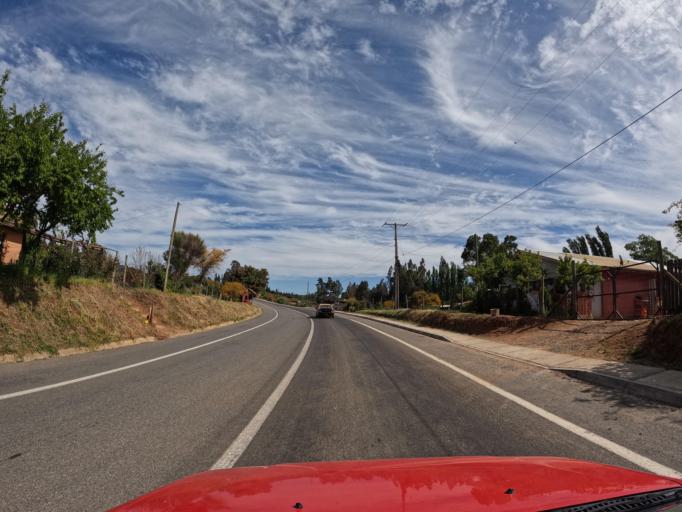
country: CL
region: Maule
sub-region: Provincia de Talca
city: Talca
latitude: -35.1177
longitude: -71.9586
